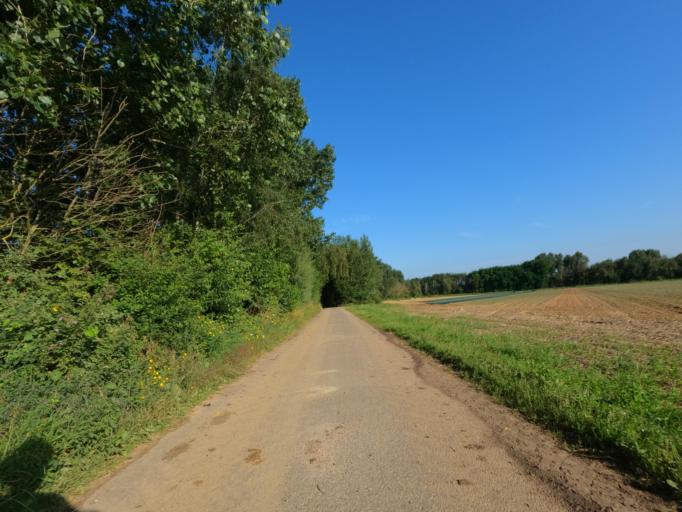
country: DE
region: North Rhine-Westphalia
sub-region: Regierungsbezirk Dusseldorf
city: Grevenbroich
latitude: 51.0989
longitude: 6.5457
